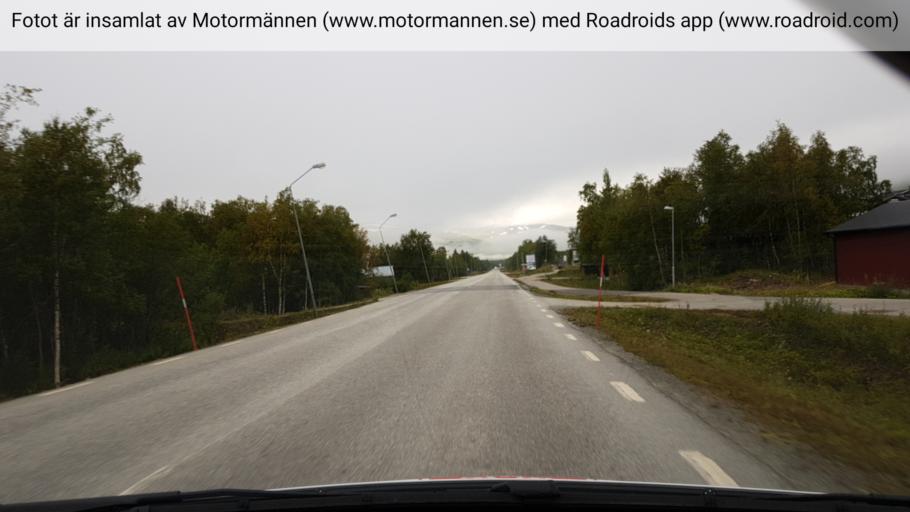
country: NO
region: Nordland
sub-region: Rana
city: Mo i Rana
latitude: 65.8270
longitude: 15.0710
